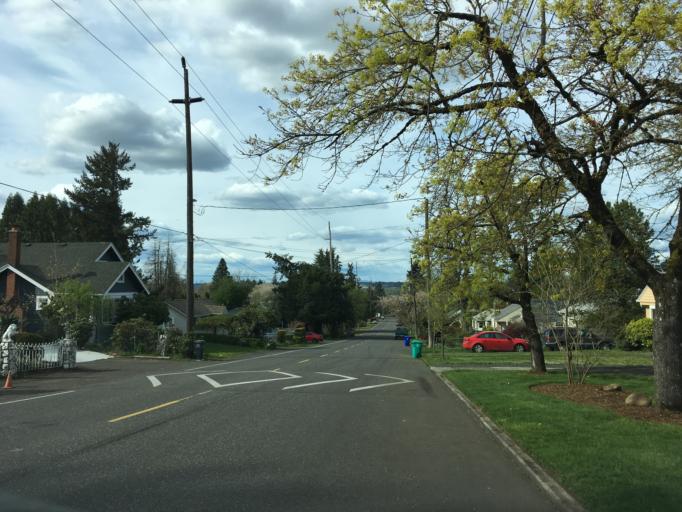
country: US
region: Oregon
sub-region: Multnomah County
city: Lents
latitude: 45.5486
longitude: -122.5475
